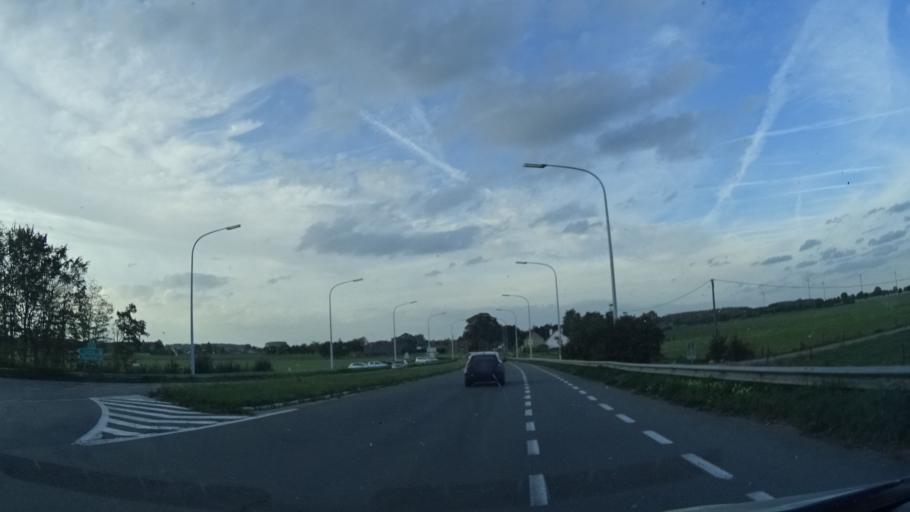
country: BE
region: Wallonia
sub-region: Province du Hainaut
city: Peruwelz
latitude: 50.5355
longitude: 3.6028
